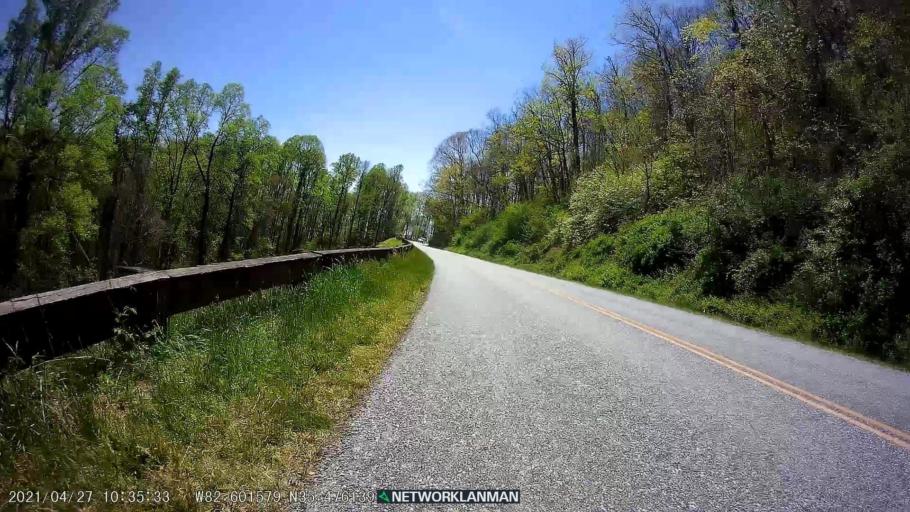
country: US
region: North Carolina
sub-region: Buncombe County
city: Avery Creek
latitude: 35.4763
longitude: -82.6015
